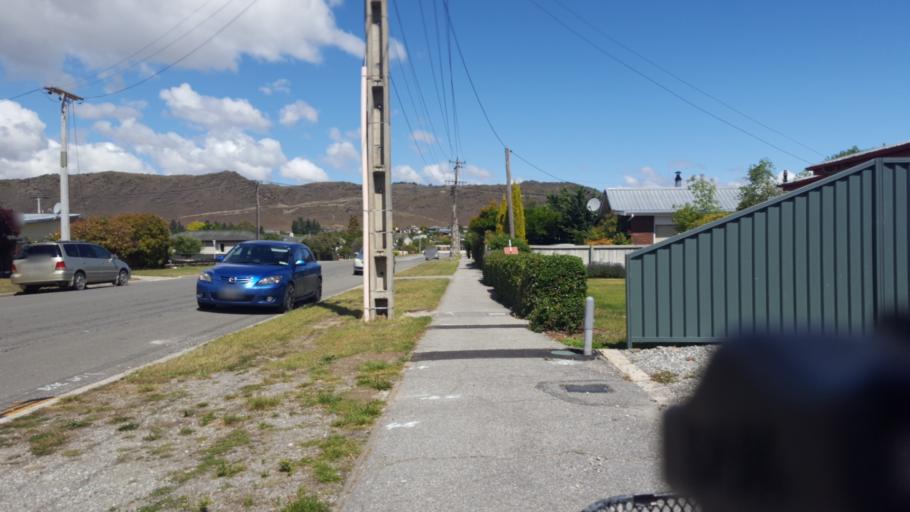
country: NZ
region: Otago
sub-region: Queenstown-Lakes District
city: Wanaka
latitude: -45.2474
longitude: 169.3948
